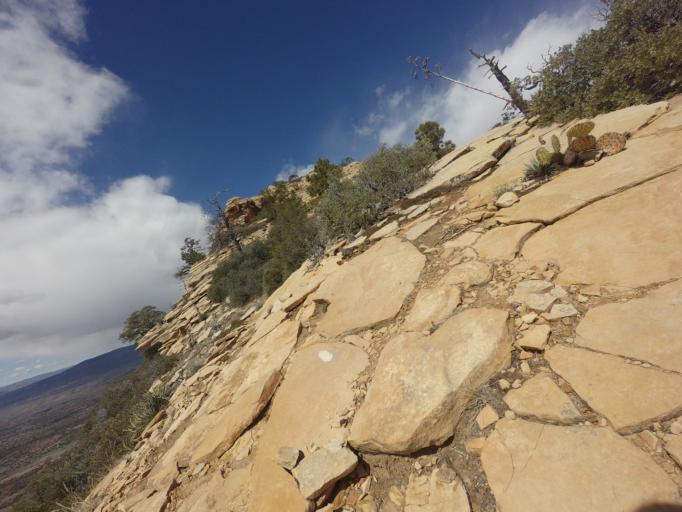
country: US
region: Arizona
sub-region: Yavapai County
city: West Sedona
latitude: 34.9119
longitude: -111.8782
